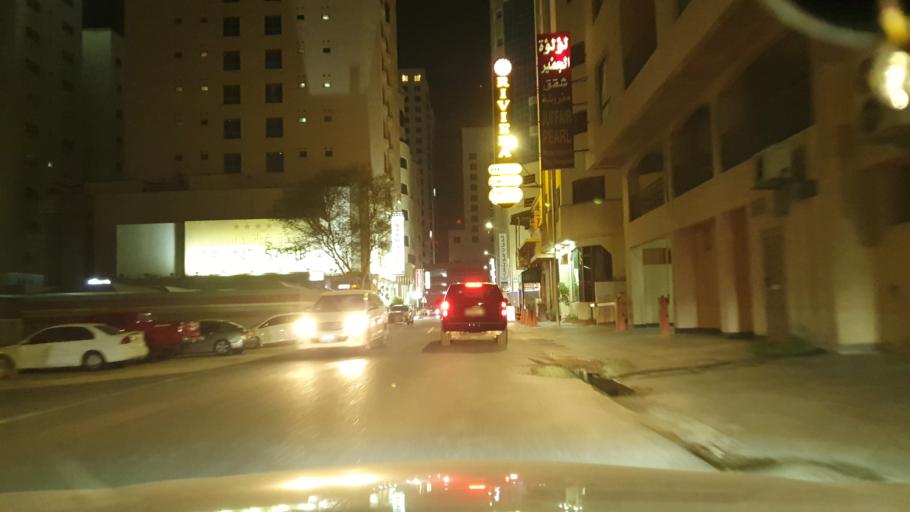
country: BH
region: Manama
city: Manama
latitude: 26.2184
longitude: 50.6044
